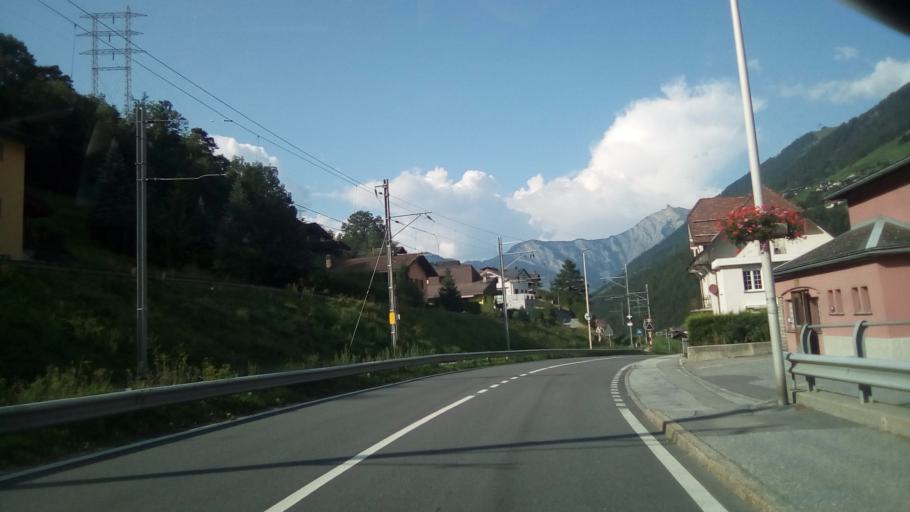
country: CH
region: Valais
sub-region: Entremont District
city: Orsieres
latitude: 46.0298
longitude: 7.1434
